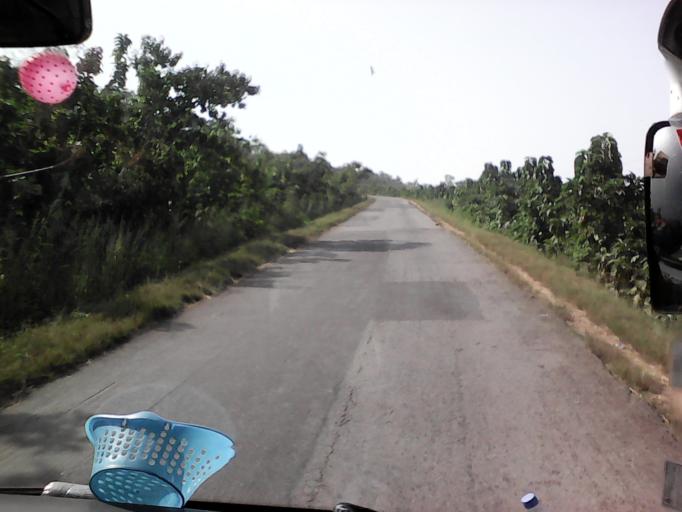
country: TG
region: Centrale
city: Sokode
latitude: 9.0553
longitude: 1.1329
